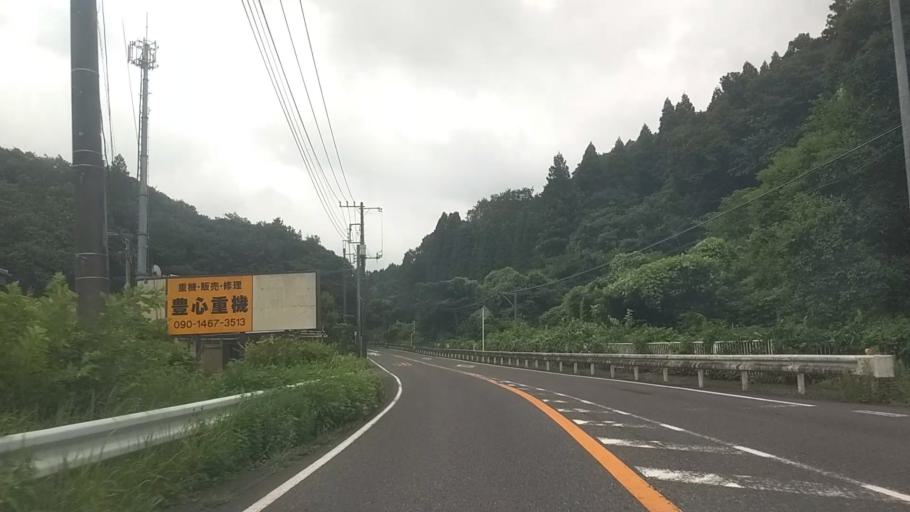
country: JP
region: Chiba
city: Kawaguchi
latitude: 35.2551
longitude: 140.0653
